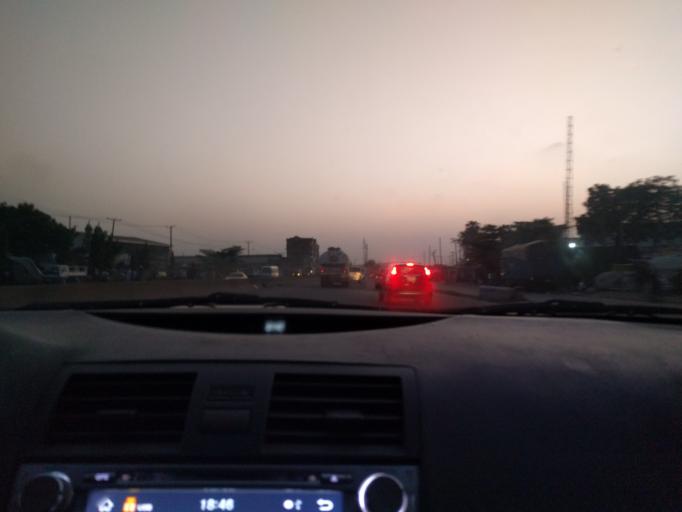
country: NG
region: Lagos
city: Mushin
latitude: 6.5156
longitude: 3.3333
